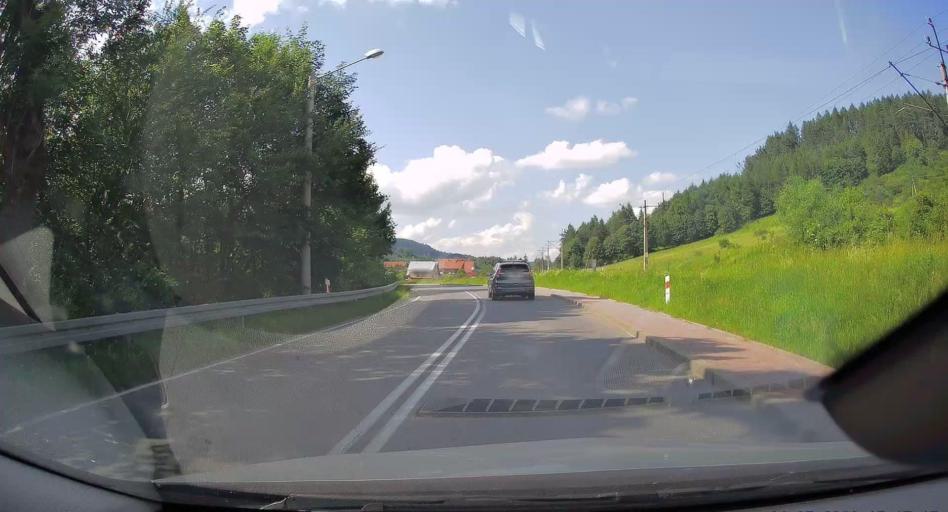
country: PL
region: Lesser Poland Voivodeship
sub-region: Powiat nowosadecki
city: Krynica-Zdroj
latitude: 49.3826
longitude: 20.9539
